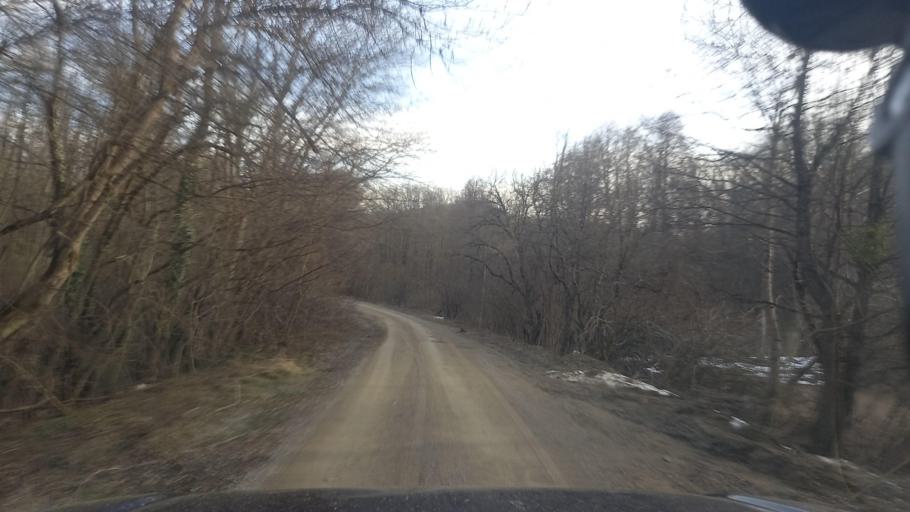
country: RU
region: Krasnodarskiy
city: Goryachiy Klyuch
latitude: 44.6942
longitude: 38.9757
